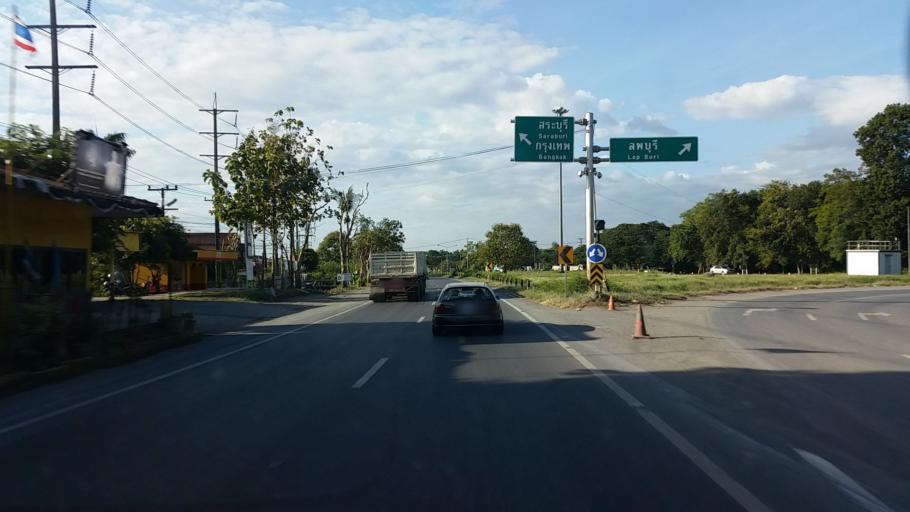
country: TH
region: Sara Buri
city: Chaloem Phra Kiat
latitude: 14.6649
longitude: 100.8886
